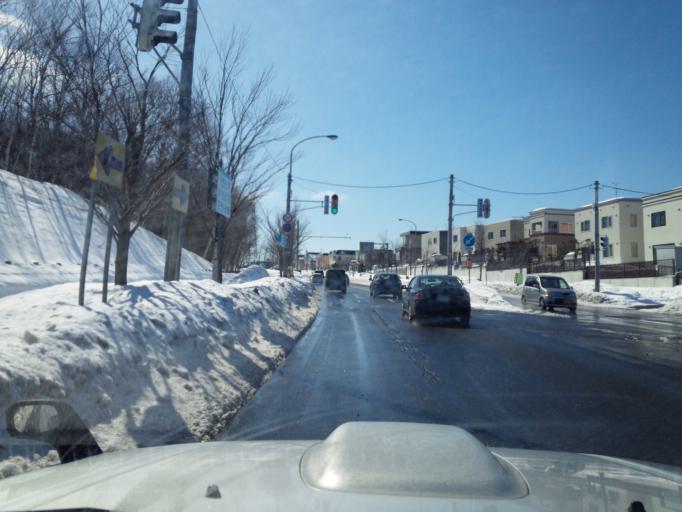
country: JP
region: Hokkaido
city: Kitahiroshima
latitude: 43.0073
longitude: 141.4624
